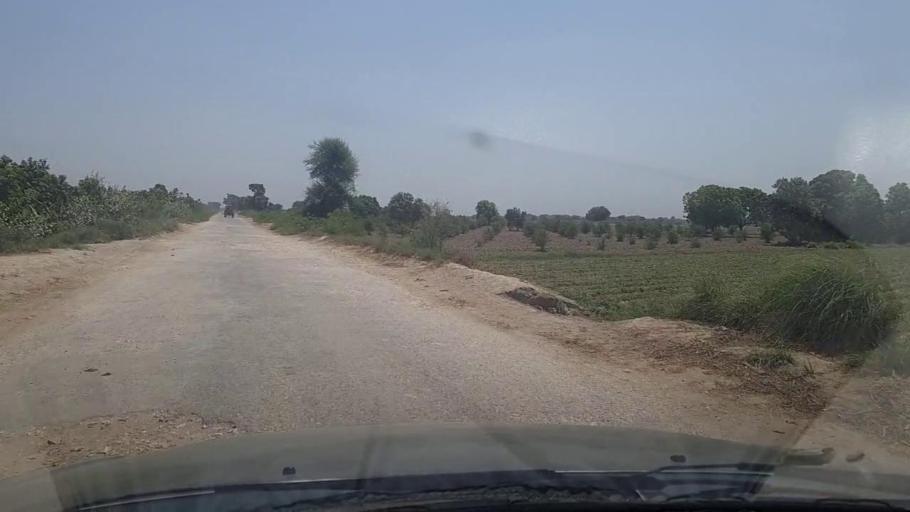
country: PK
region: Sindh
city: Tando Muhammad Khan
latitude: 25.2741
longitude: 68.6256
